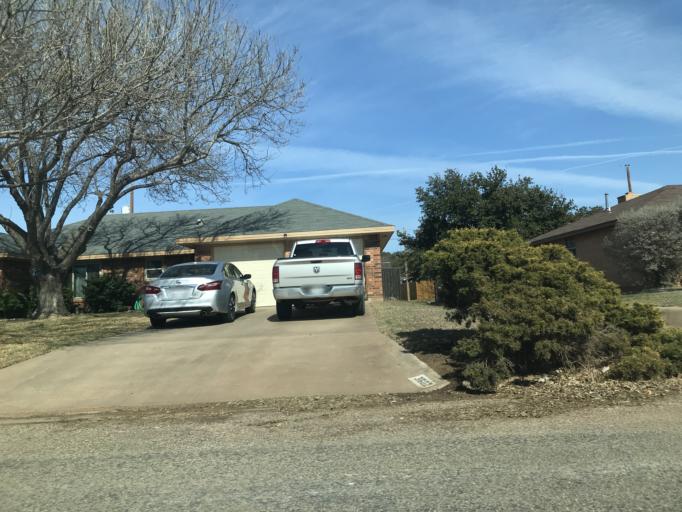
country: US
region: Texas
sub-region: Tom Green County
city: San Angelo
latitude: 31.4379
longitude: -100.4852
